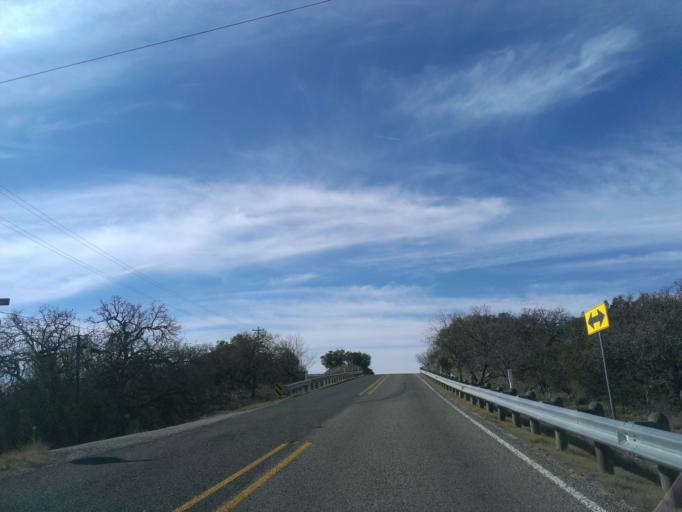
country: US
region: Texas
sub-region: Burnet County
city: Granite Shoals
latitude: 30.6018
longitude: -98.4197
